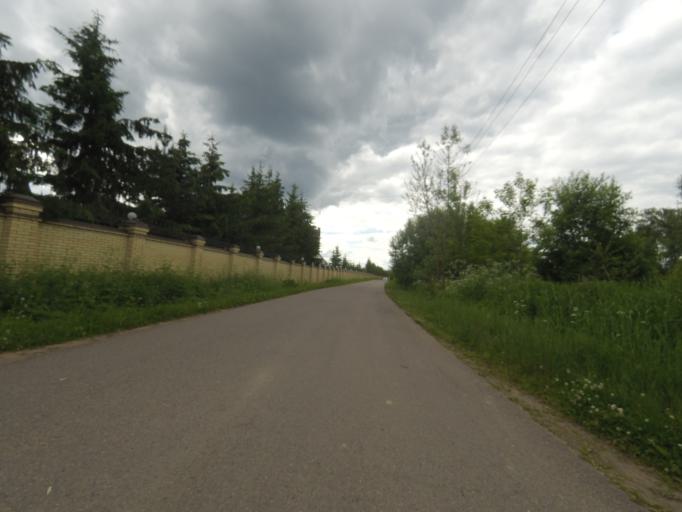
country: RU
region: Moskovskaya
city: Marfino
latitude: 56.0485
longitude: 37.6636
